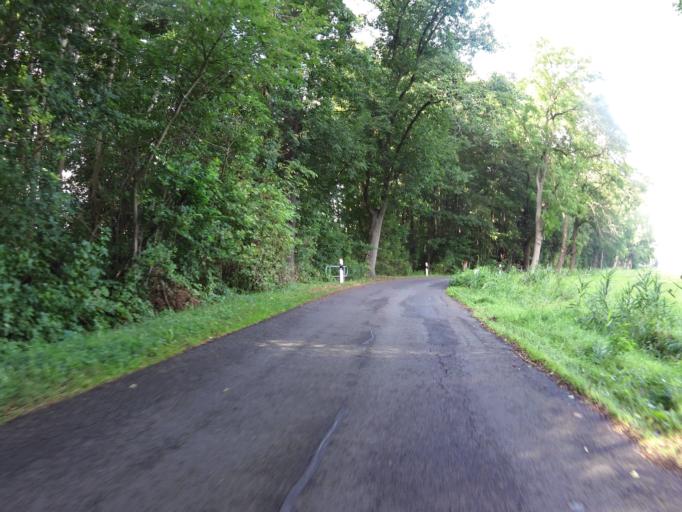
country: DE
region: Brandenburg
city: Storkow
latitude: 52.2326
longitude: 13.9329
